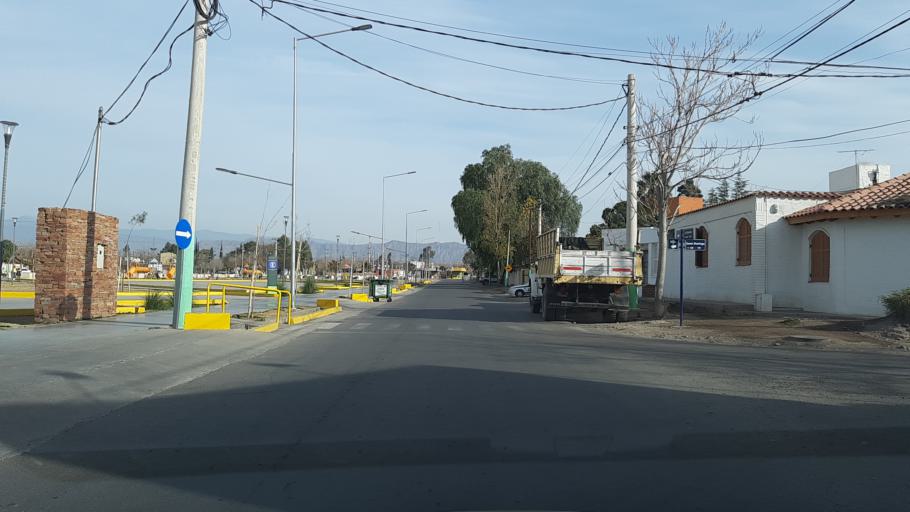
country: AR
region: San Juan
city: San Juan
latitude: -31.5321
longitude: -68.5916
